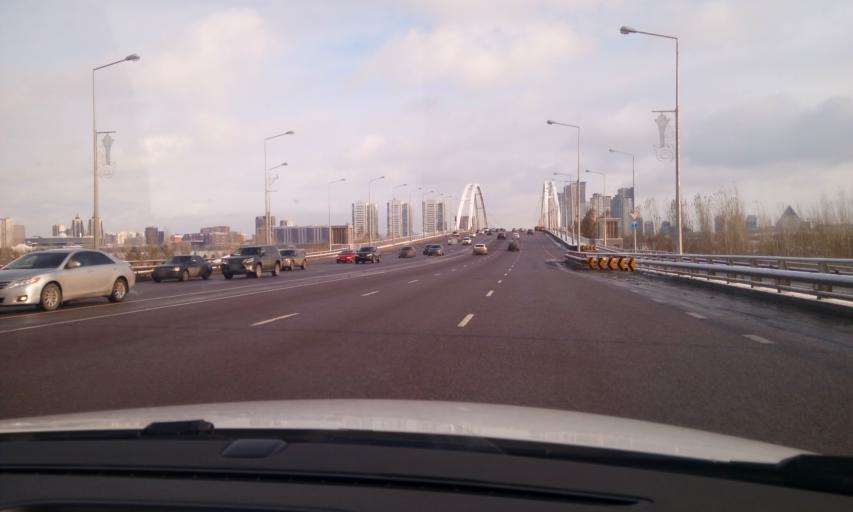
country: KZ
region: Astana Qalasy
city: Astana
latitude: 51.1320
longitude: 71.4416
